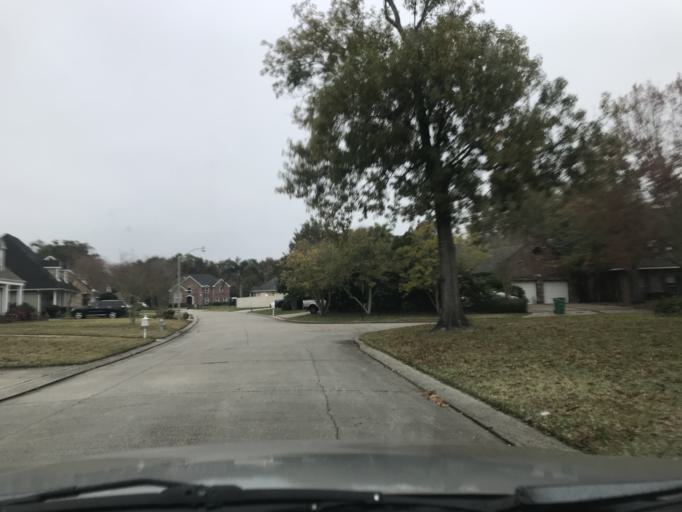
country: US
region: Louisiana
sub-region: Jefferson Parish
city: Woodmere
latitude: 29.8717
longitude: -90.0919
